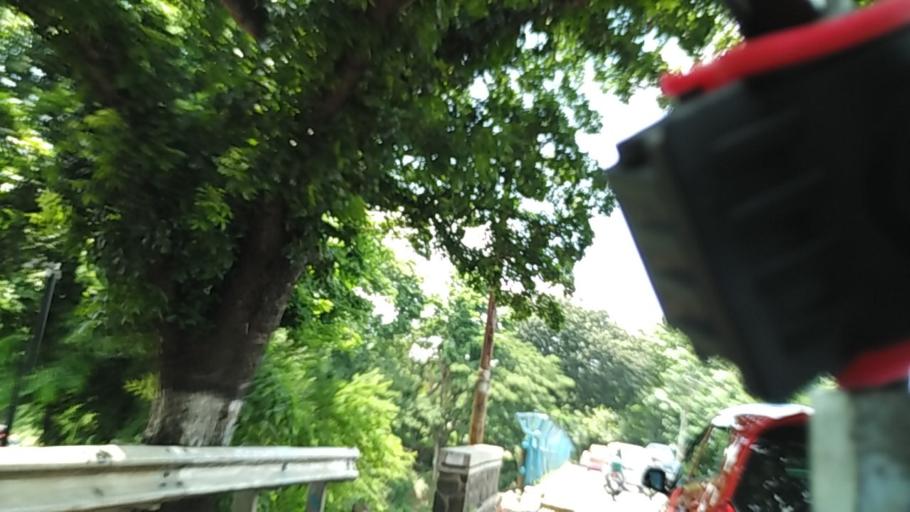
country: ID
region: Central Java
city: Semarang
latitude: -7.0066
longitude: 110.3789
